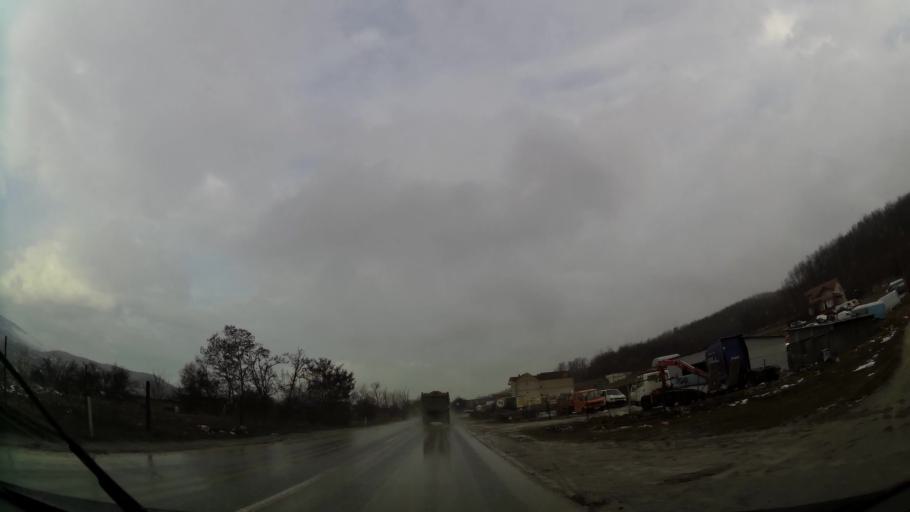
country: XK
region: Ferizaj
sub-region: Komuna e Kacanikut
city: Kacanik
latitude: 42.2427
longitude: 21.2423
